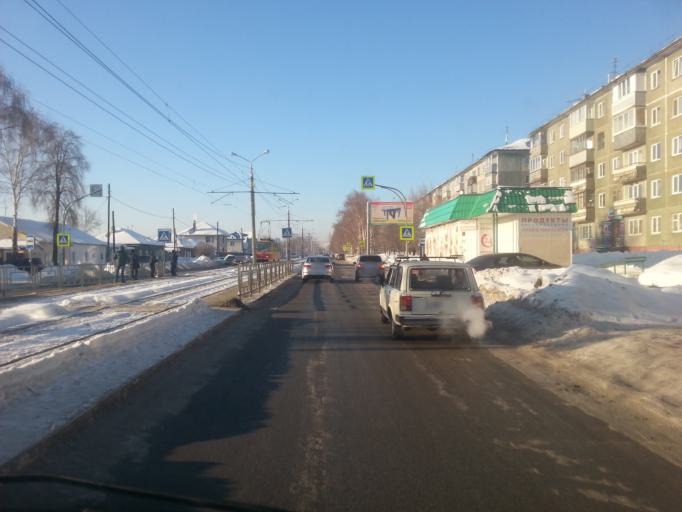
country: RU
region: Altai Krai
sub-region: Gorod Barnaulskiy
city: Barnaul
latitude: 53.3517
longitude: 83.7291
